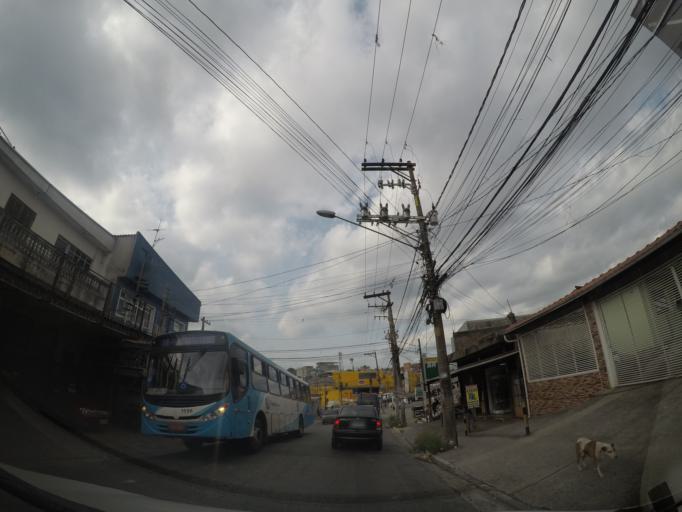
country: BR
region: Sao Paulo
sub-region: Guarulhos
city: Guarulhos
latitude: -23.4208
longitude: -46.5060
